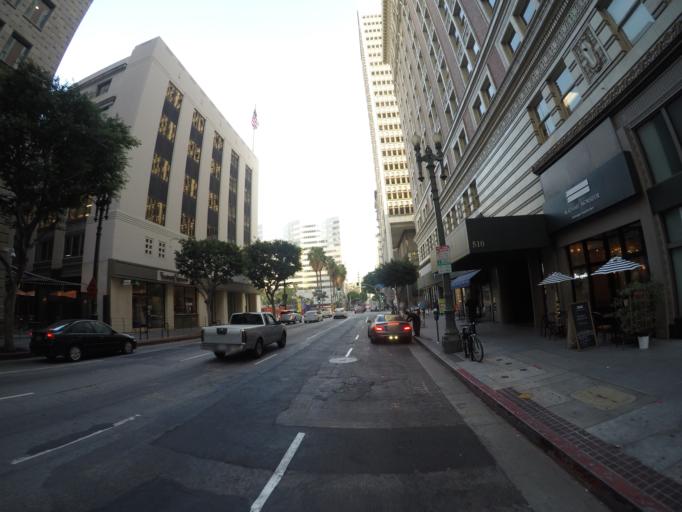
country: US
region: California
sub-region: Los Angeles County
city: Los Angeles
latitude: 34.0483
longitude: -118.2546
